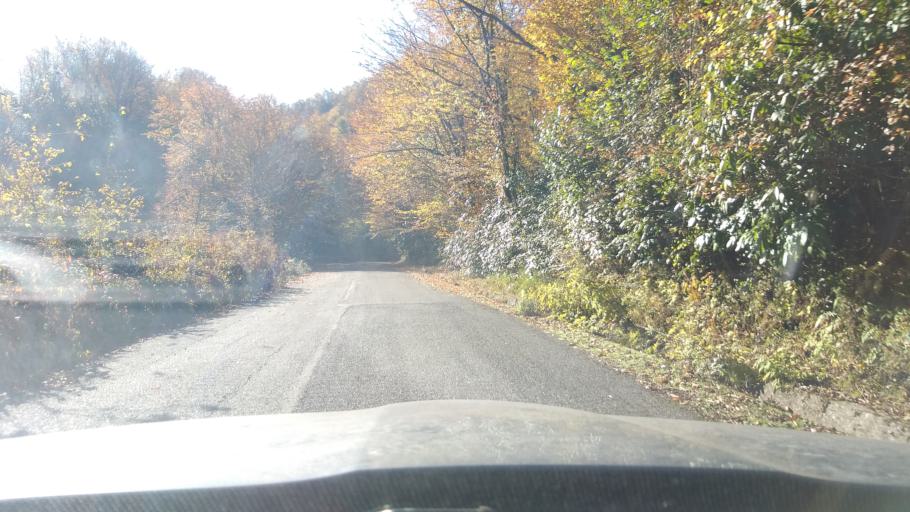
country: GE
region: Abkhazia
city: Bich'vinta
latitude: 43.1896
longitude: 40.4542
